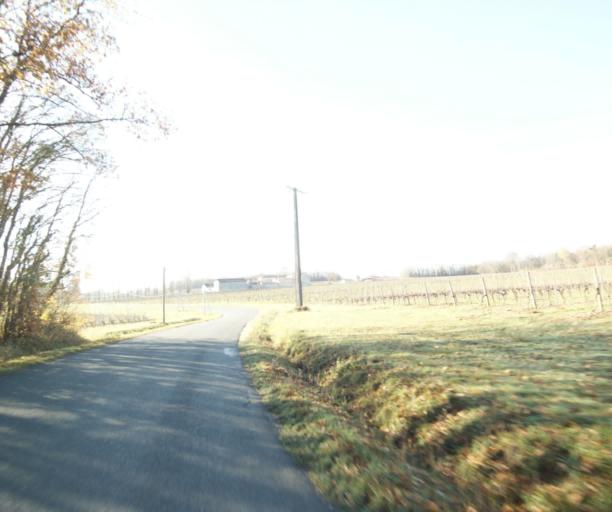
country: FR
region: Poitou-Charentes
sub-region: Departement de la Charente-Maritime
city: Cherac
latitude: 45.7307
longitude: -0.4527
